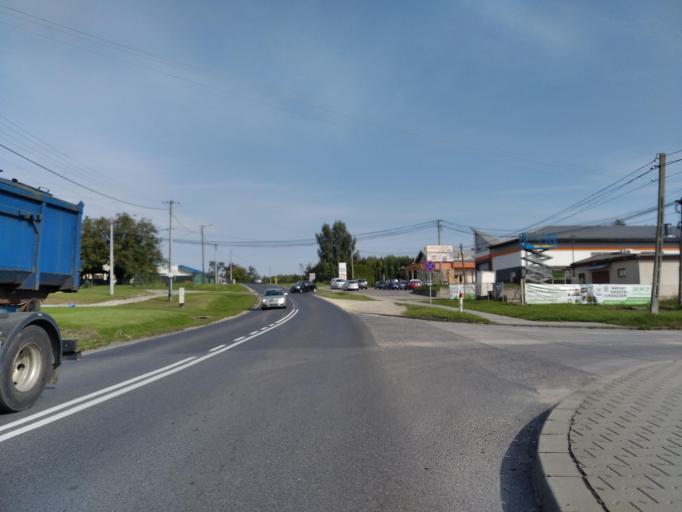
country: PL
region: Subcarpathian Voivodeship
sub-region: Powiat ropczycko-sedziszowski
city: Ostrow
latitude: 50.1000
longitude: 21.5934
